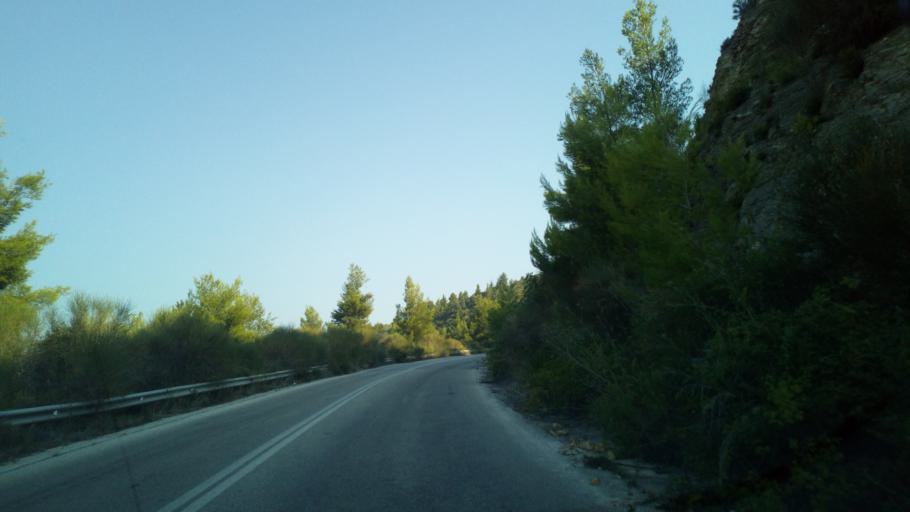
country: GR
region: Central Macedonia
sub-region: Nomos Chalkidikis
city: Neos Marmaras
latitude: 40.1713
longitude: 23.8596
